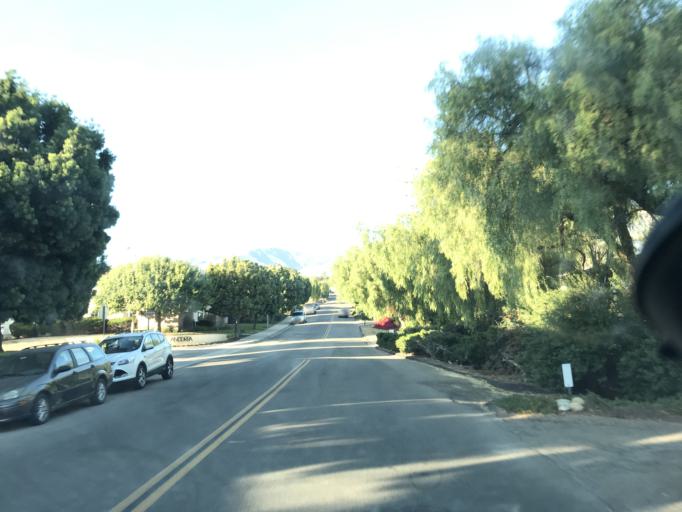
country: US
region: California
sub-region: Santa Barbara County
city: Mission Canyon
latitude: 34.4538
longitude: -119.7598
